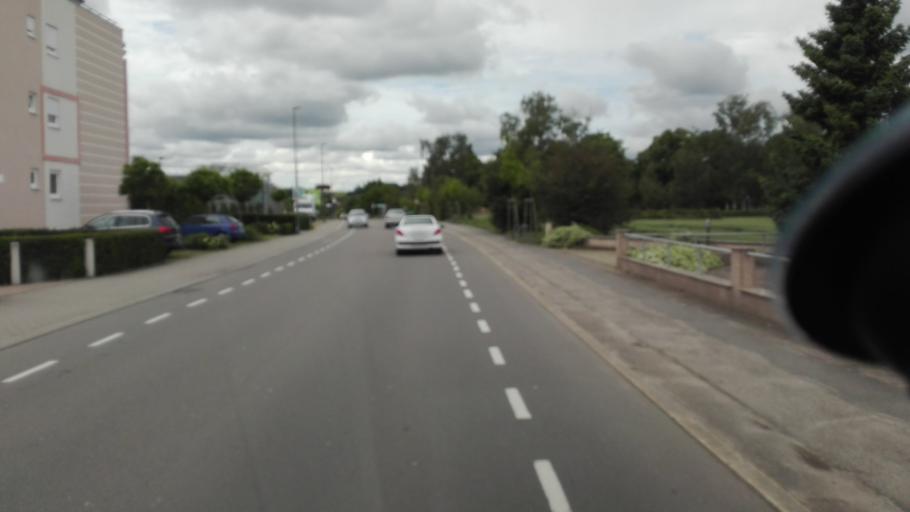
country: DE
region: Baden-Wuerttemberg
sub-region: Karlsruhe Region
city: Wiesloch
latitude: 49.2885
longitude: 8.6950
